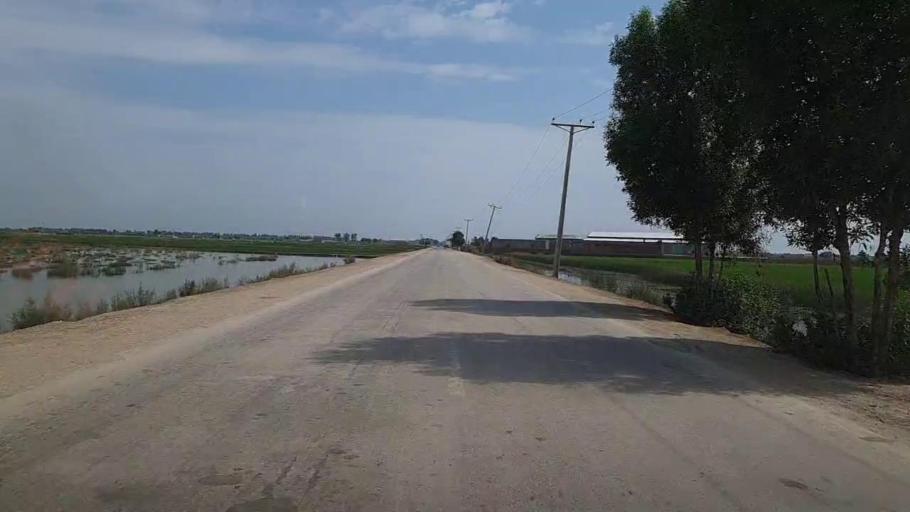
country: PK
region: Sindh
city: Thul
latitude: 28.2553
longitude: 68.7794
